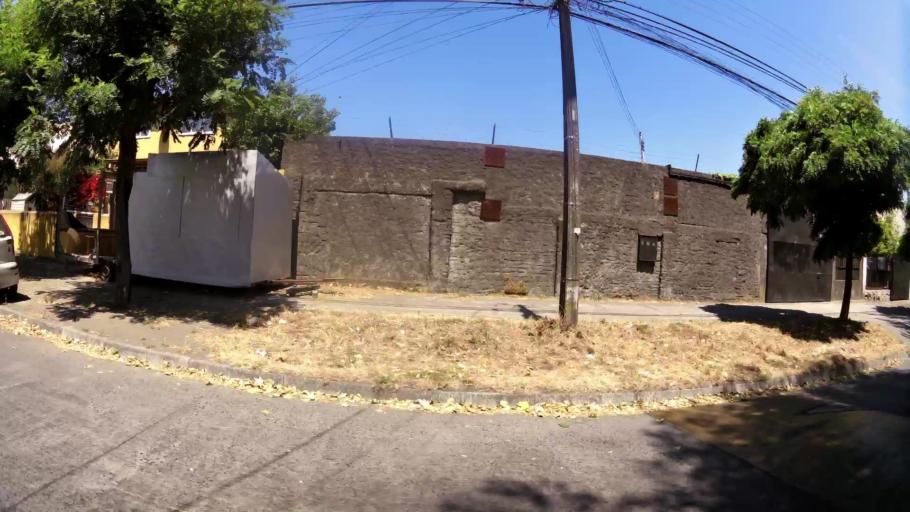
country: CL
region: Biobio
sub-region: Provincia de Concepcion
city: Concepcion
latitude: -36.8046
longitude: -73.0505
